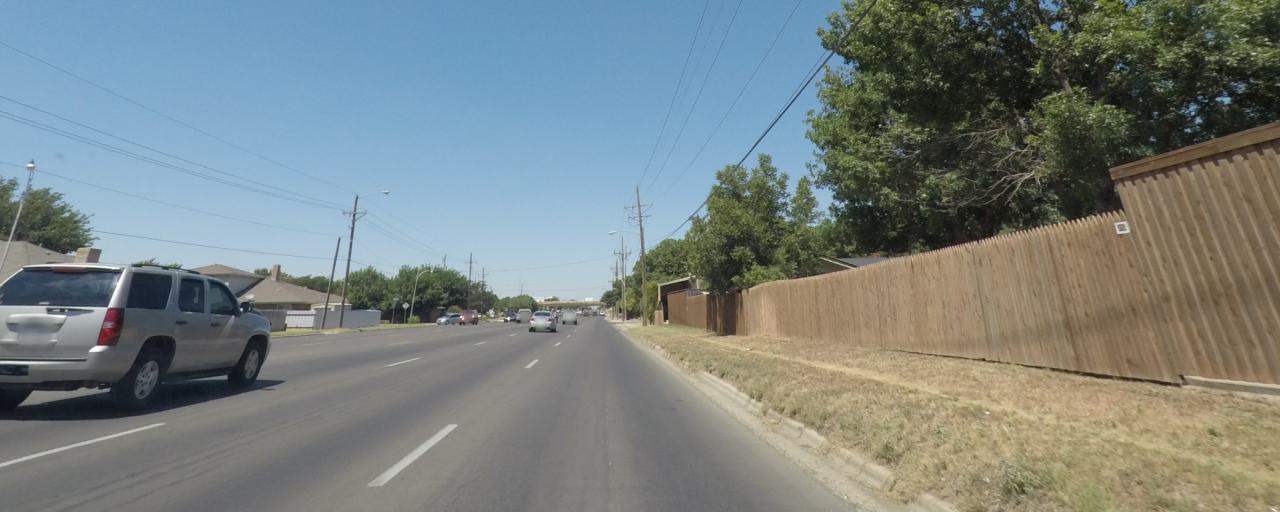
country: US
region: Texas
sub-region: Lubbock County
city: Lubbock
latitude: 33.5256
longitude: -101.8876
